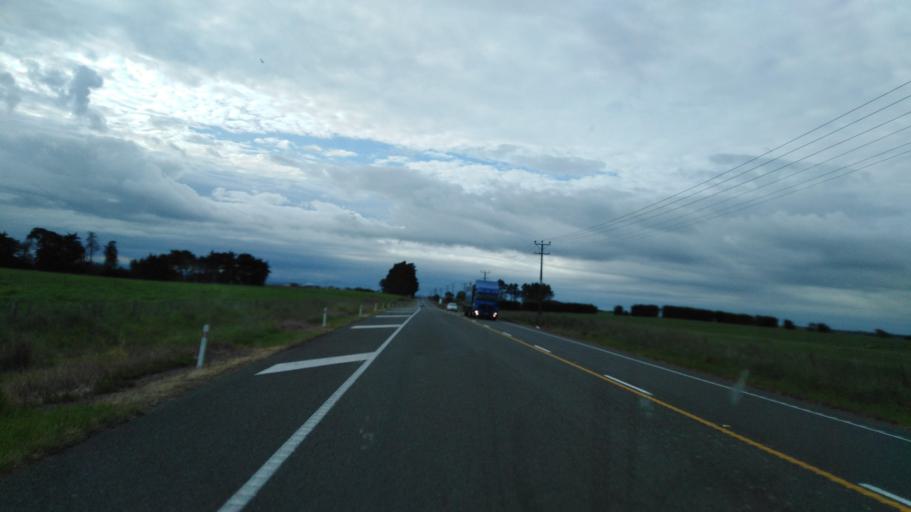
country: NZ
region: Manawatu-Wanganui
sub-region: Rangitikei District
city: Bulls
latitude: -40.1361
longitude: 175.3642
